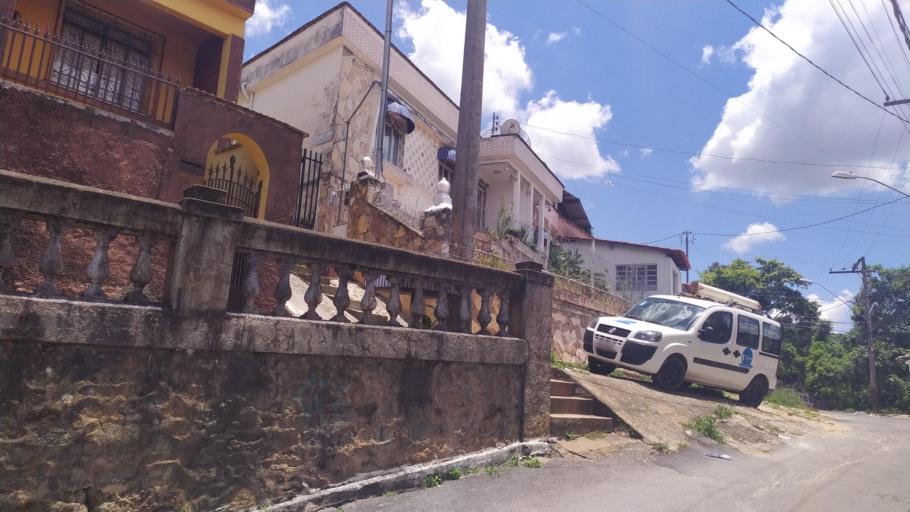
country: BR
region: Minas Gerais
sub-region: Sao Joao Del Rei
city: Sao Joao del Rei
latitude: -21.1334
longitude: -44.2636
